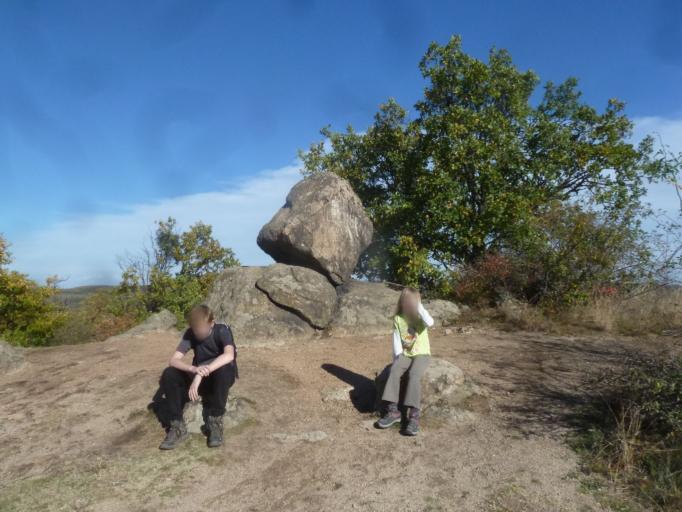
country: HU
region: Fejer
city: Pakozd
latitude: 47.2370
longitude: 18.5385
